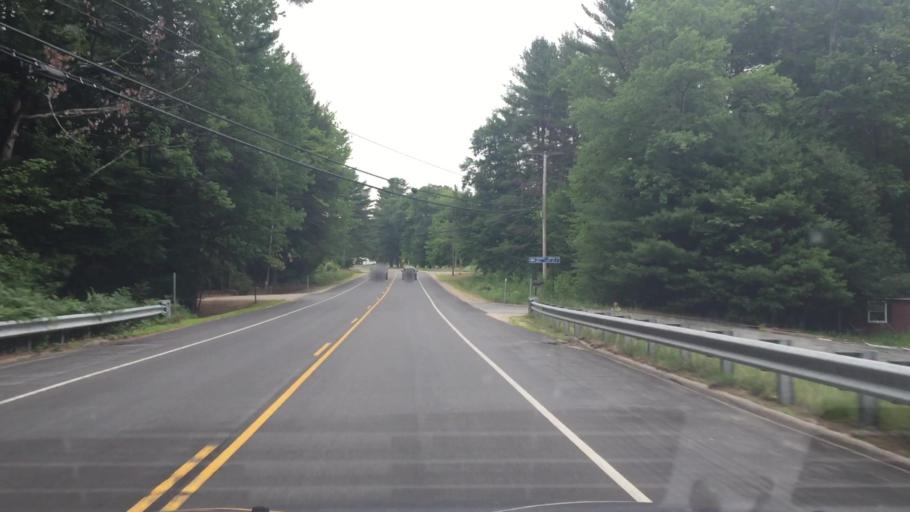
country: US
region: New Hampshire
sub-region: Carroll County
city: Tamworth
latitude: 43.8473
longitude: -71.2652
